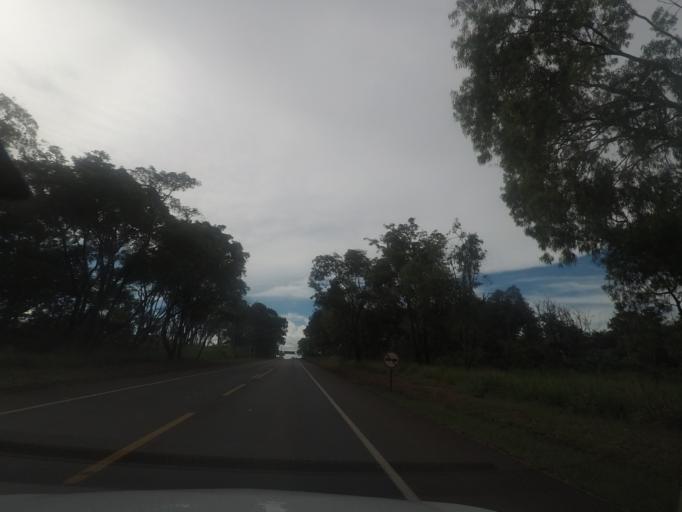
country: BR
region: Minas Gerais
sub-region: Prata
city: Prata
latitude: -19.2742
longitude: -48.9180
